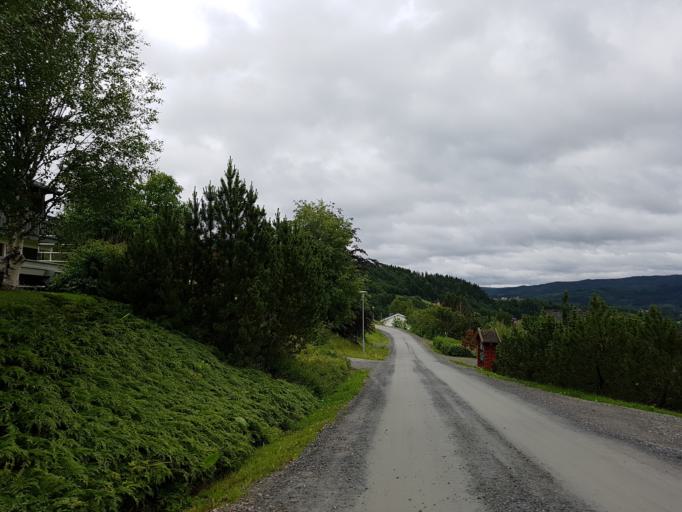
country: NO
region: Sor-Trondelag
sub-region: Selbu
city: Mebonden
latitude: 63.2234
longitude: 11.0379
